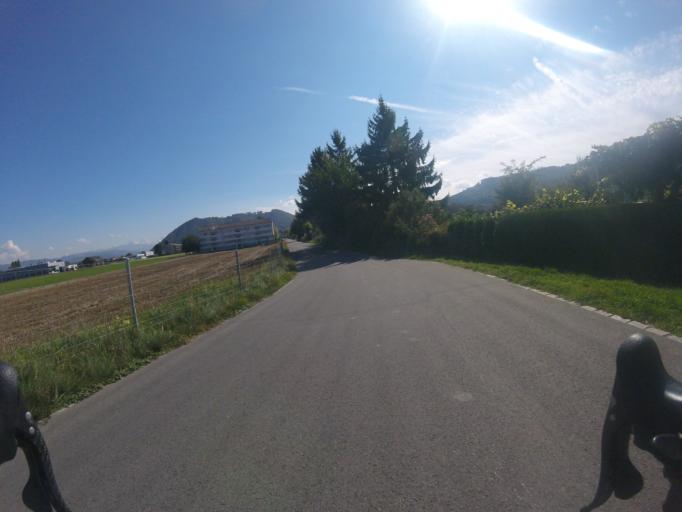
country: CH
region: Bern
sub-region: Bern-Mittelland District
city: Belp
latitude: 46.9041
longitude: 7.4985
